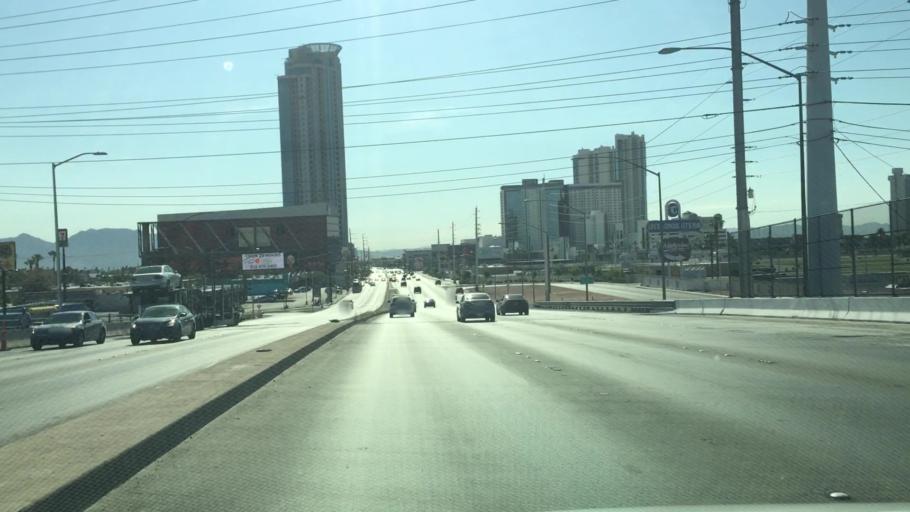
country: US
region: Nevada
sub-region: Clark County
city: Las Vegas
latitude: 36.1439
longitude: -115.1652
